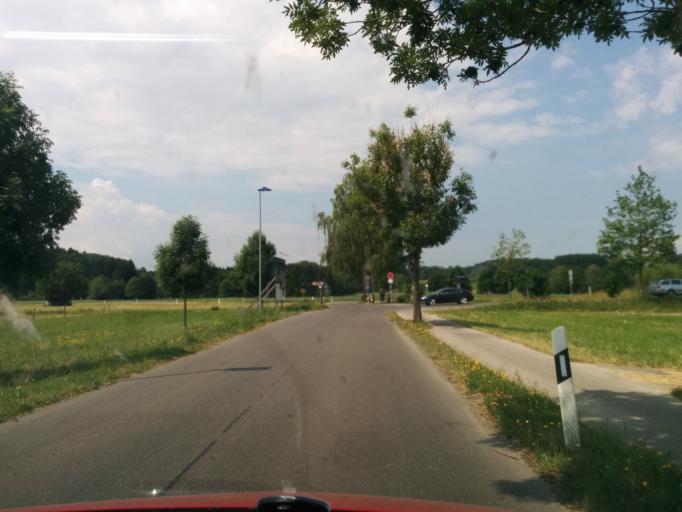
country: DE
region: Bavaria
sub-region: Swabia
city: Bad Worishofen
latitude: 48.0184
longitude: 10.5941
